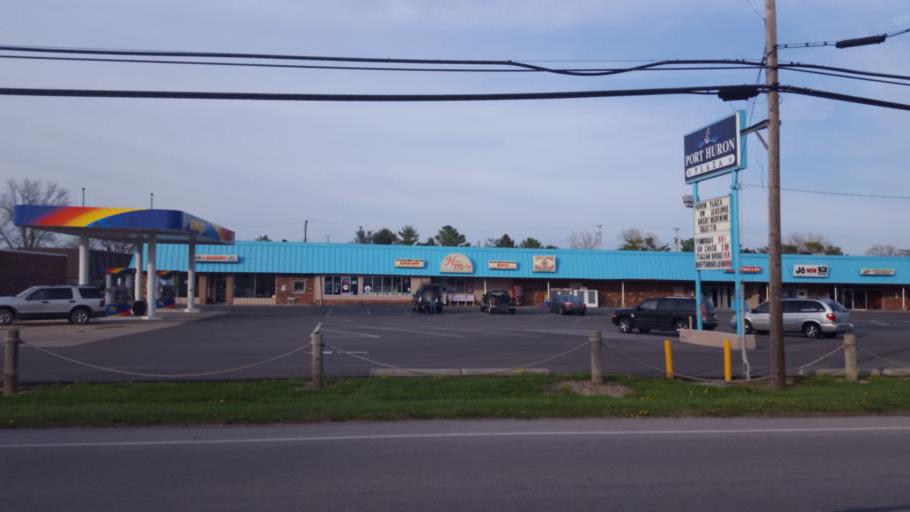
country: US
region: Ohio
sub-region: Erie County
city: Huron
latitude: 41.3985
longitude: -82.5612
